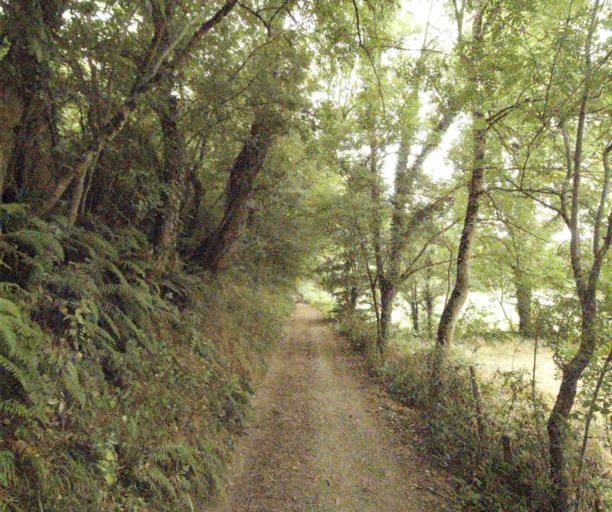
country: FR
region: Midi-Pyrenees
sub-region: Departement du Tarn
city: Soreze
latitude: 43.4396
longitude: 2.0610
